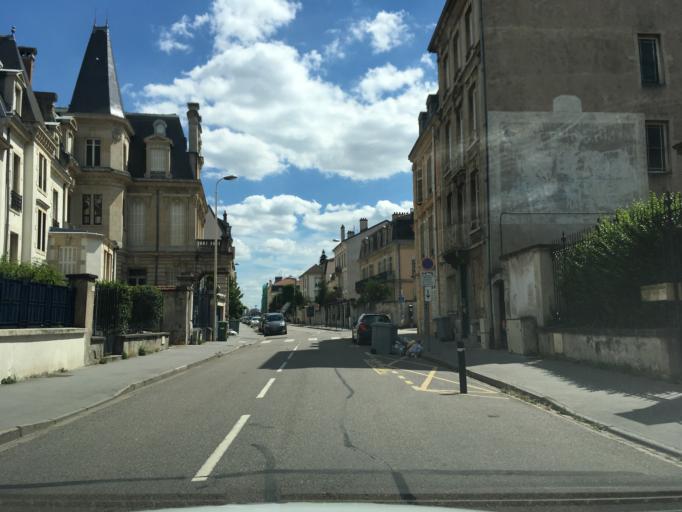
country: FR
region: Lorraine
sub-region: Departement de Meurthe-et-Moselle
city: Maxeville
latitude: 48.6950
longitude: 6.1705
